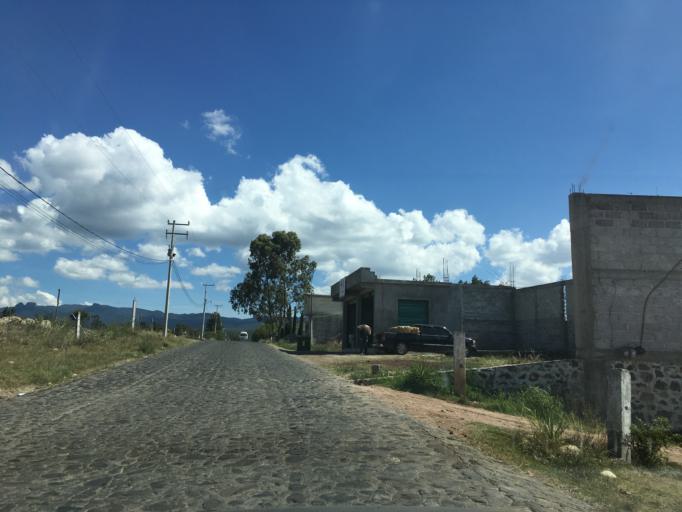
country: MX
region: Hidalgo
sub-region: Omitlan de Juarez
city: San Antonio el Paso
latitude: 20.2290
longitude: -98.5560
